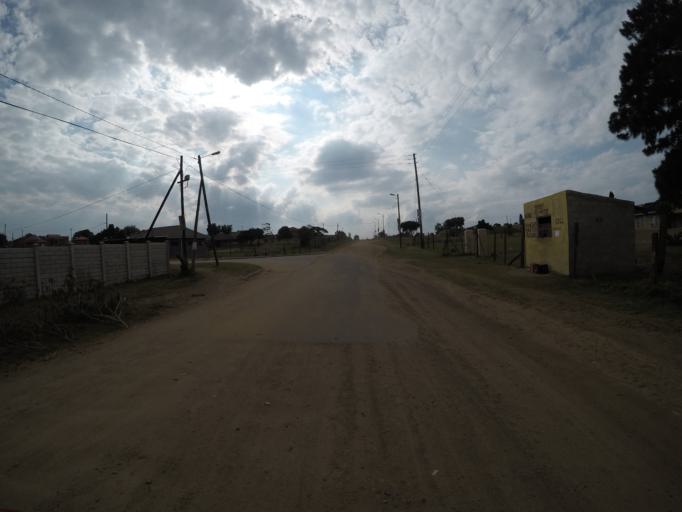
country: ZA
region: KwaZulu-Natal
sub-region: uThungulu District Municipality
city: Richards Bay
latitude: -28.7442
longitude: 32.1045
